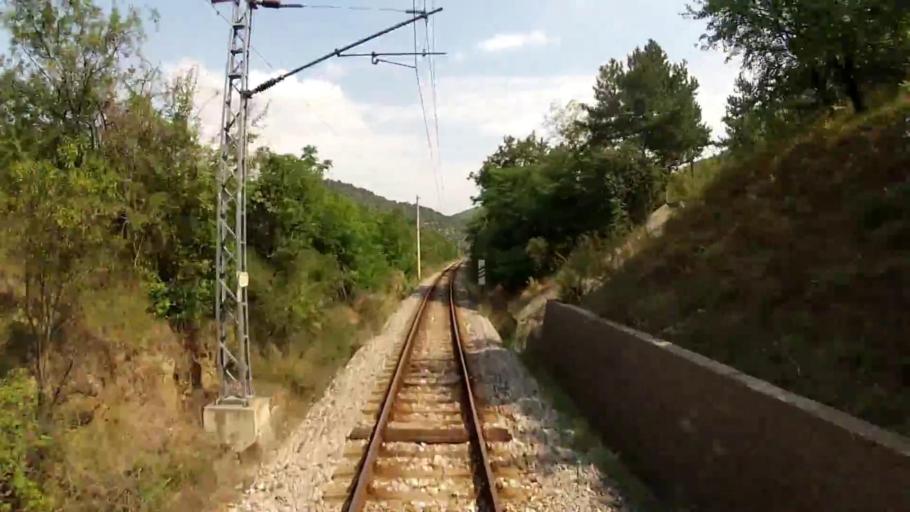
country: BG
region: Blagoevgrad
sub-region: Obshtina Kresna
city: Kresna
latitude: 41.7187
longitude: 23.1656
